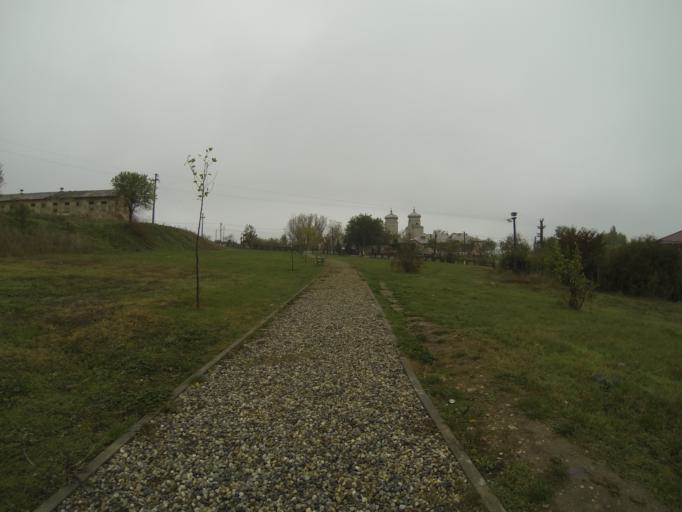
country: RO
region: Dolj
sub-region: Comuna Segarcea
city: Segarcea
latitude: 44.0965
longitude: 23.7432
